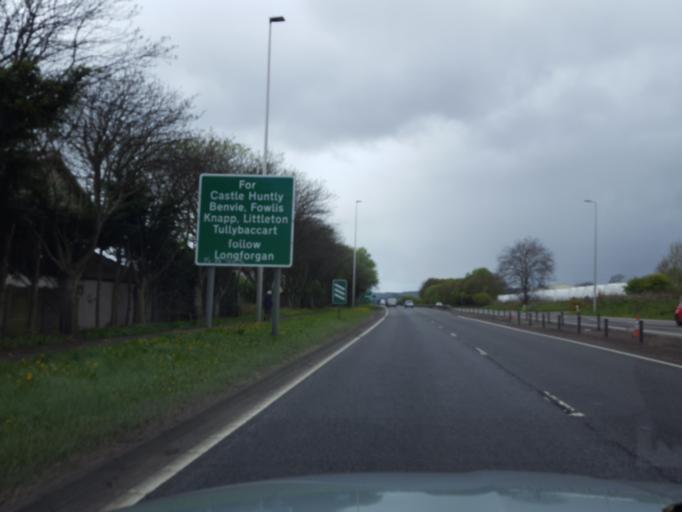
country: GB
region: Scotland
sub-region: Angus
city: Muirhead
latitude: 56.4589
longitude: -3.1165
